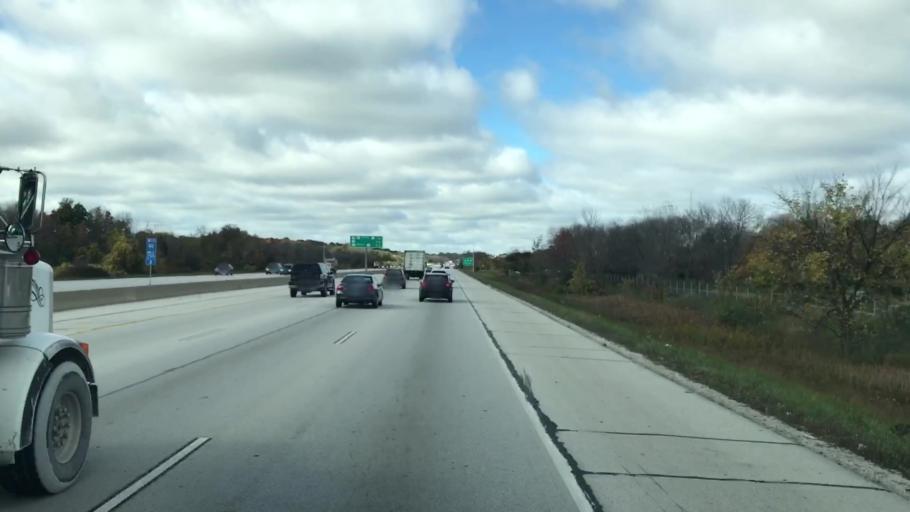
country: US
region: Wisconsin
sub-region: Waukesha County
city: Brookfield
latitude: 43.0291
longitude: -88.1355
